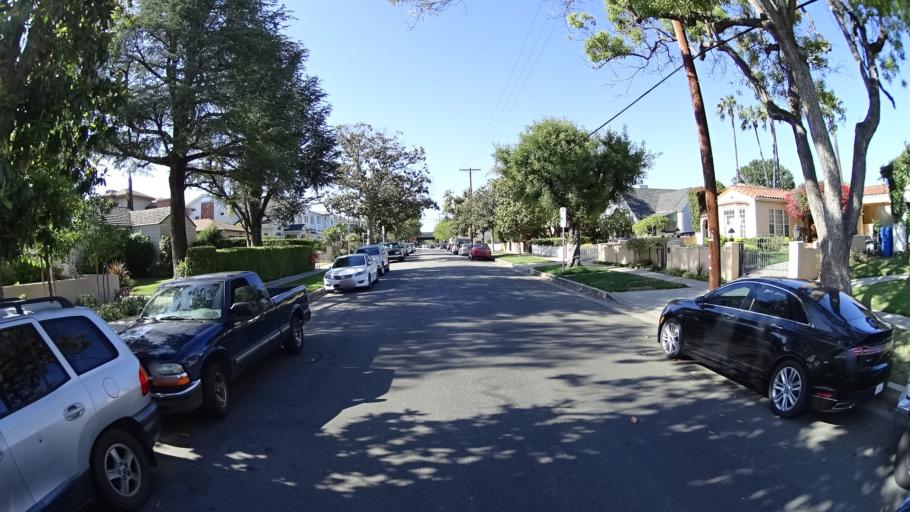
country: US
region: California
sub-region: Los Angeles County
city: Universal City
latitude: 34.1508
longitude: -118.3527
